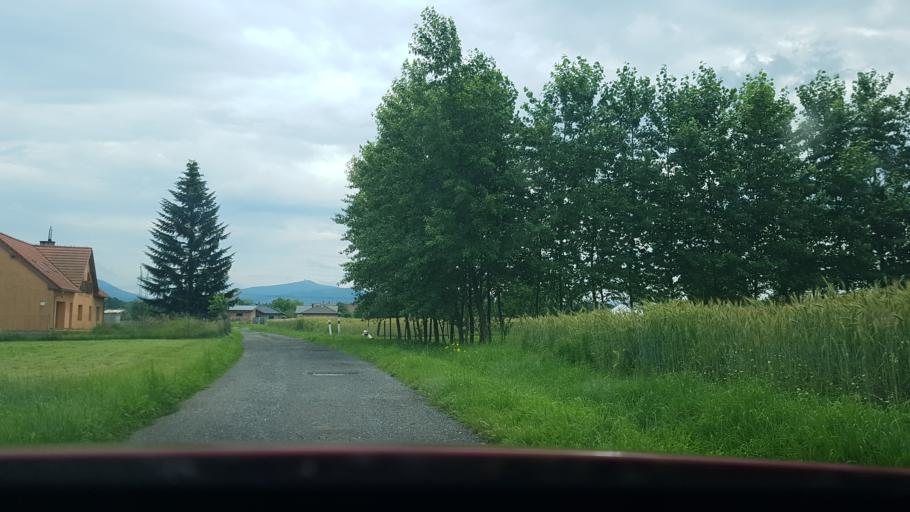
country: CZ
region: Moravskoslezsky
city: Lucina
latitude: 49.6930
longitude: 18.4451
